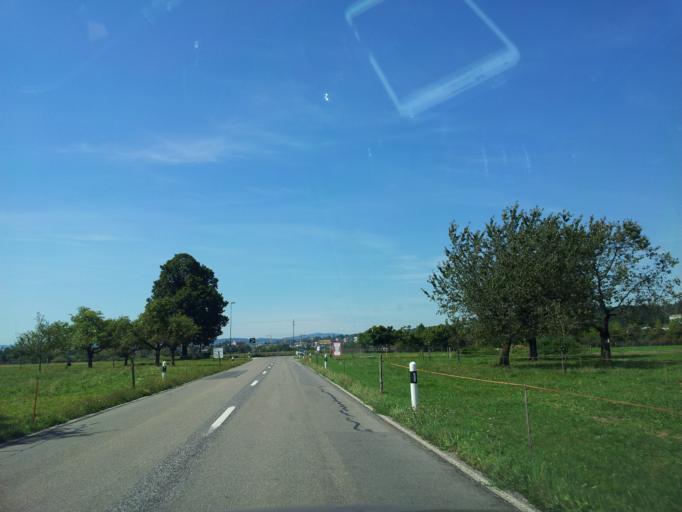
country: CH
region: Saint Gallen
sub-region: Wahlkreis See-Gaster
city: Jona
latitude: 47.2210
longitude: 8.8685
